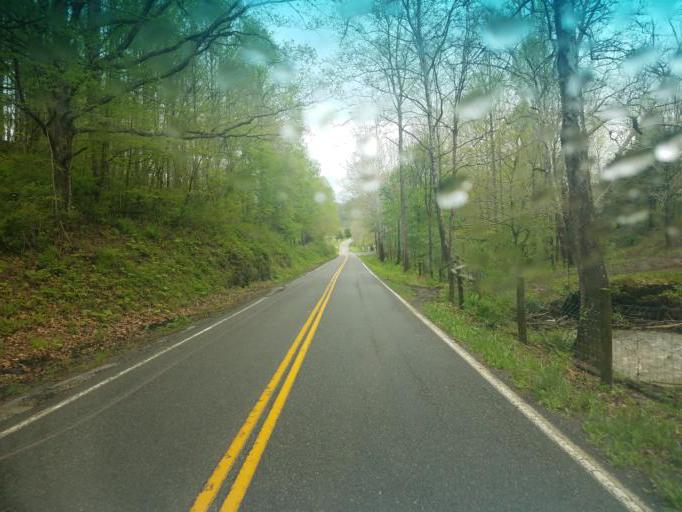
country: US
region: Virginia
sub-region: Smyth County
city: Marion
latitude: 36.9456
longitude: -81.5315
